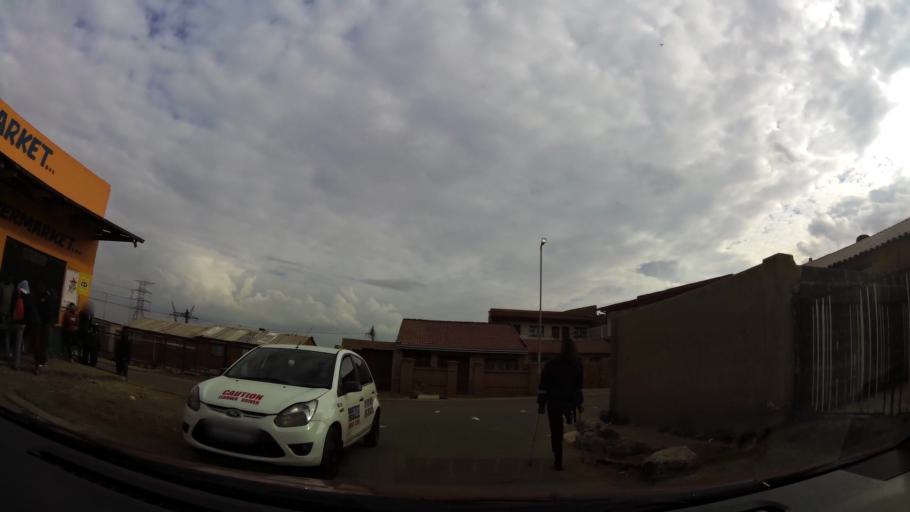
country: ZA
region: Gauteng
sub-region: City of Johannesburg Metropolitan Municipality
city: Soweto
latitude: -26.2465
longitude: 27.8378
